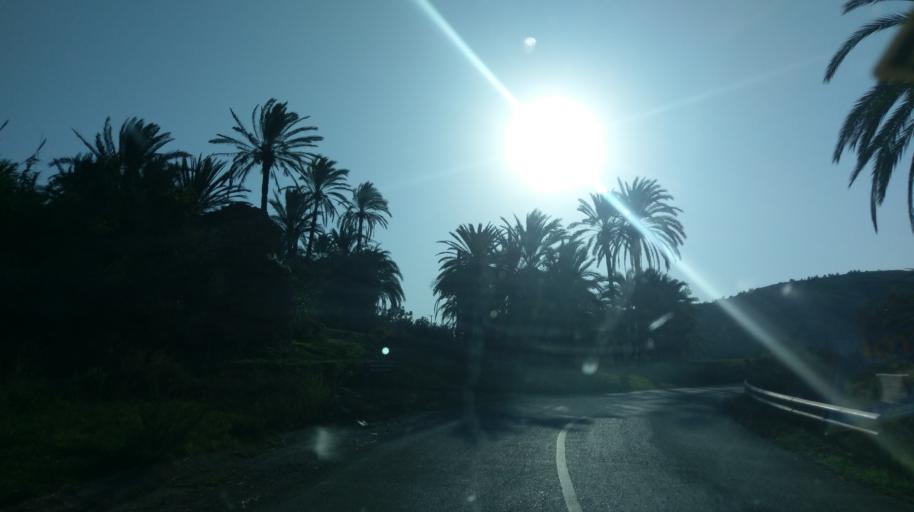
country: CY
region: Lefkosia
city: Lefka
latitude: 35.1006
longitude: 32.8463
